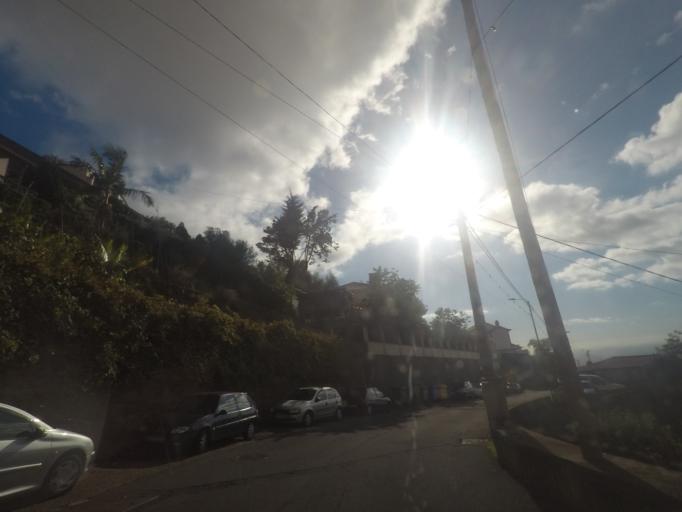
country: PT
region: Madeira
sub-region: Funchal
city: Nossa Senhora do Monte
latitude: 32.6574
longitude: -16.8756
